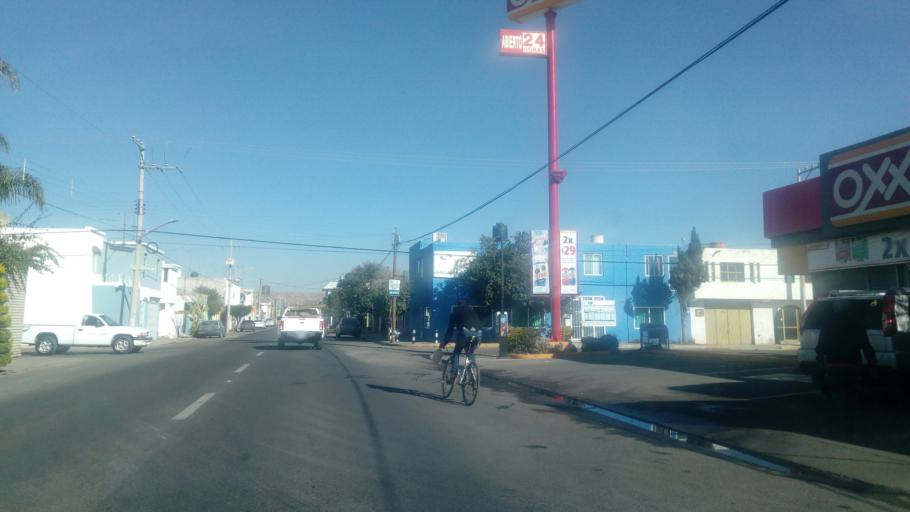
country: MX
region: Durango
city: Victoria de Durango
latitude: 24.0334
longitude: -104.6595
